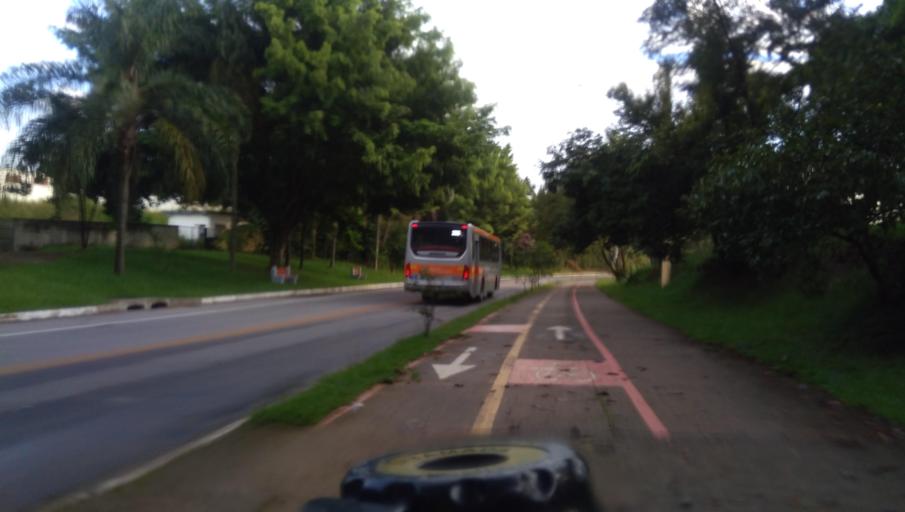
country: BR
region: Sao Paulo
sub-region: Sao Jose Dos Campos
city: Sao Jose dos Campos
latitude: -23.1461
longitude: -45.7956
